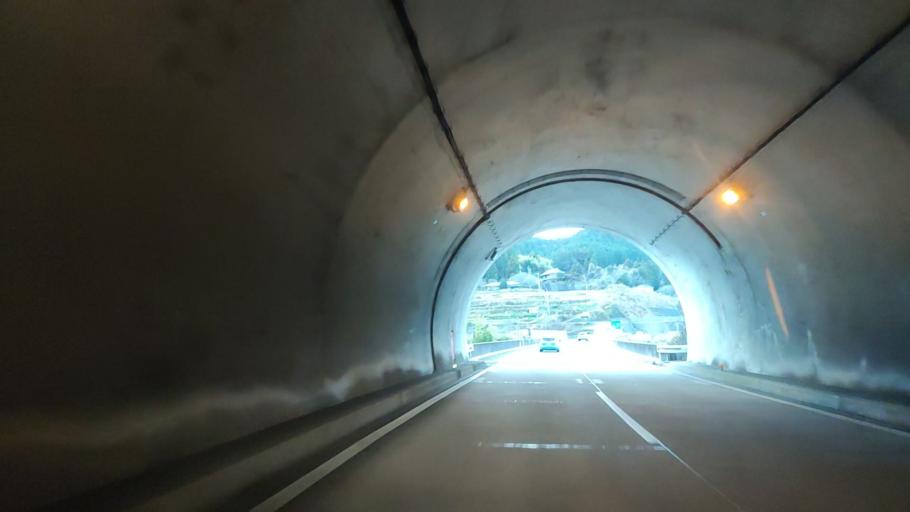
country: JP
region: Ehime
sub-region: Shikoku-chuo Shi
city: Matsuyama
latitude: 33.7899
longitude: 132.9209
